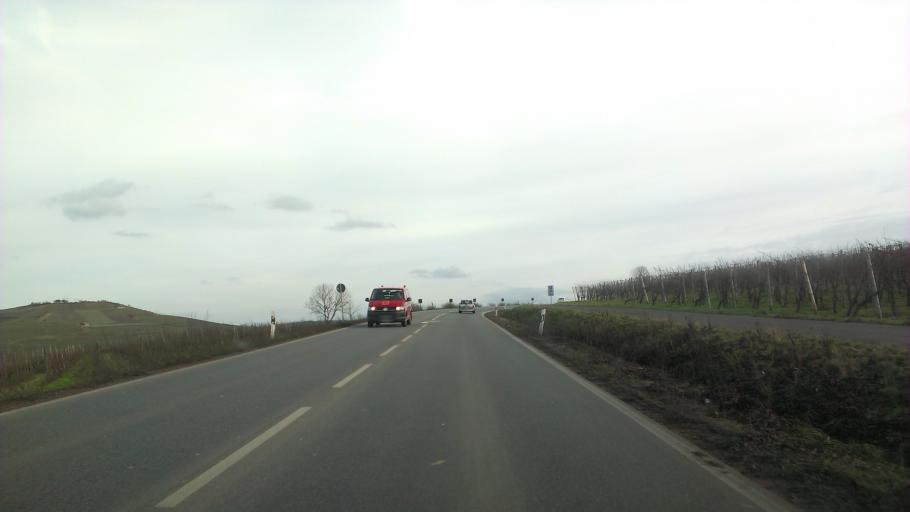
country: DE
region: Rheinland-Pfalz
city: Bretzenheim
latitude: 49.8501
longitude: 7.9039
